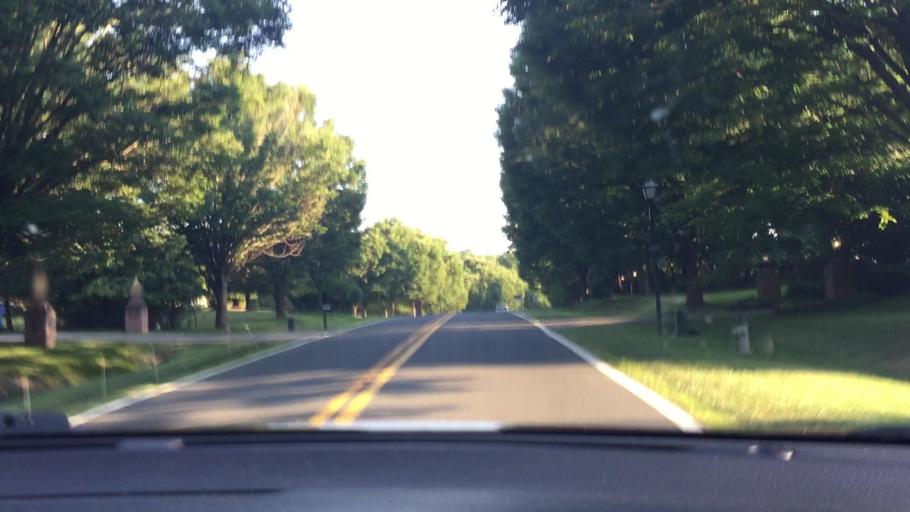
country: US
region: Maryland
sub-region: Montgomery County
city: Potomac
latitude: 39.0203
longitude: -77.1813
